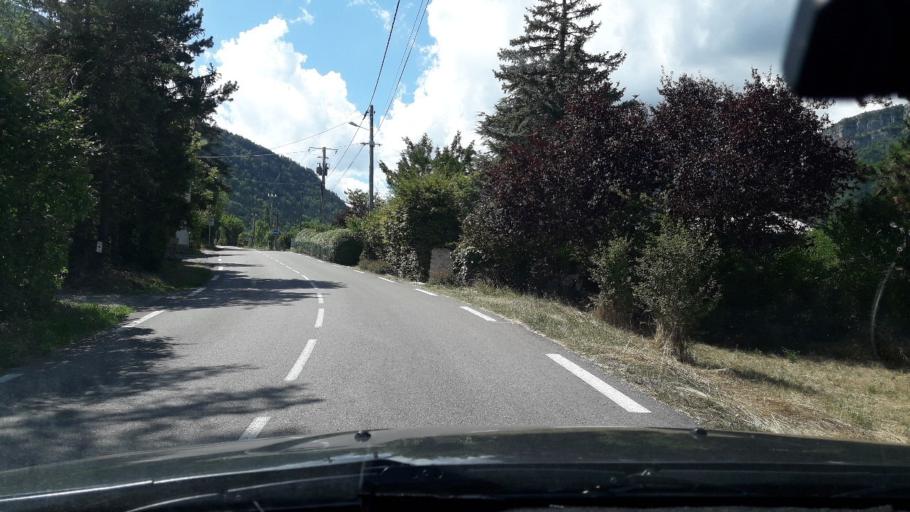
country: FR
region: Rhone-Alpes
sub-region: Departement de l'Isere
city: Mens
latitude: 44.8288
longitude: 5.6138
